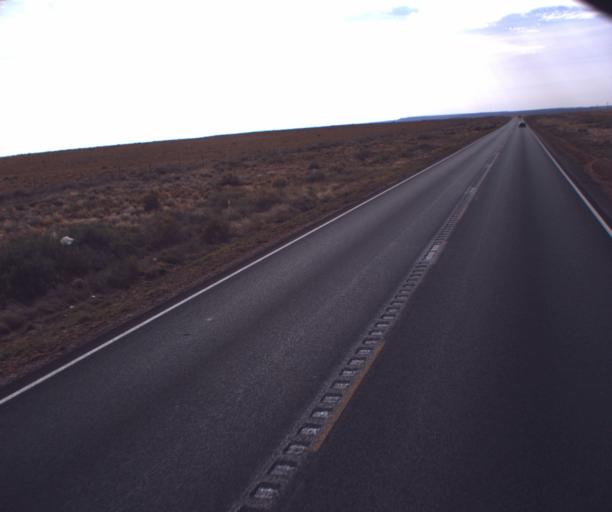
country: US
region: Arizona
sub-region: Apache County
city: Chinle
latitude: 36.0260
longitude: -109.6061
